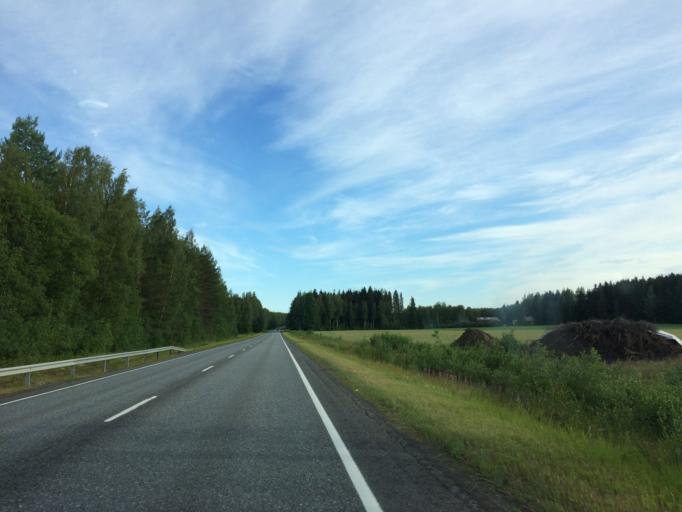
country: FI
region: Haeme
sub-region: Haemeenlinna
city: Janakkala
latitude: 60.9305
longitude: 24.5300
